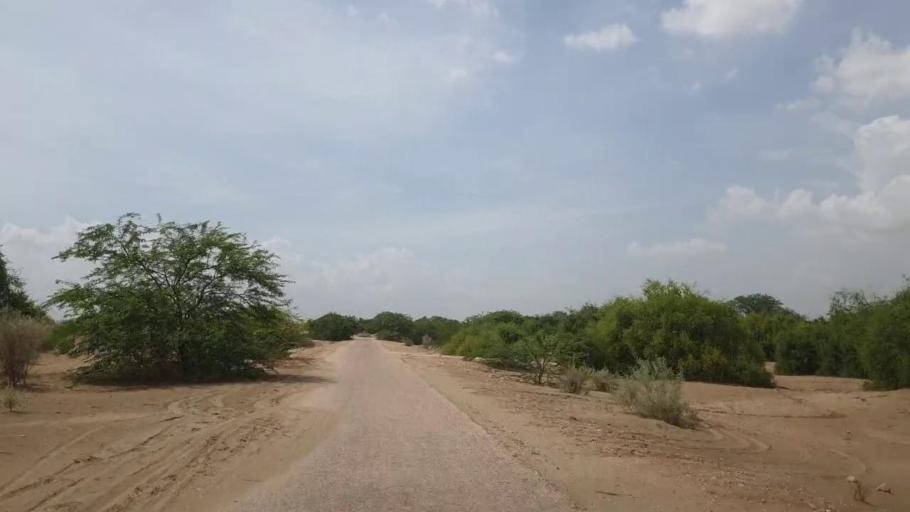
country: PK
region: Sindh
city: Kot Diji
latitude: 27.2340
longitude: 69.0880
